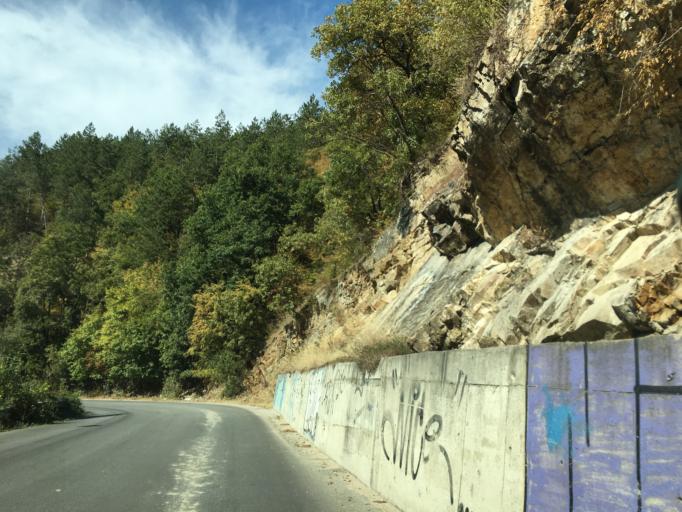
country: BG
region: Pazardzhik
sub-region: Obshtina Peshtera
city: Peshtera
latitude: 42.0176
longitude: 24.2738
